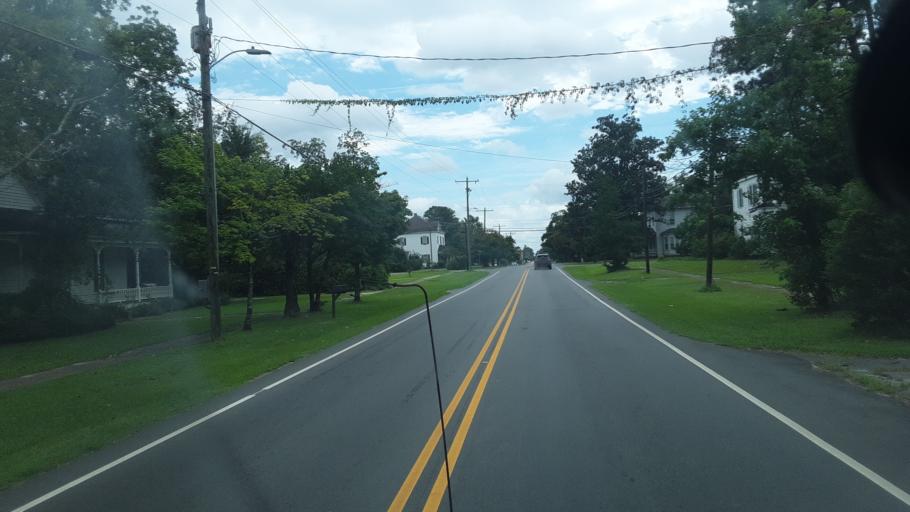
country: US
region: North Carolina
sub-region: Robeson County
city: Rowland
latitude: 34.5400
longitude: -79.2990
